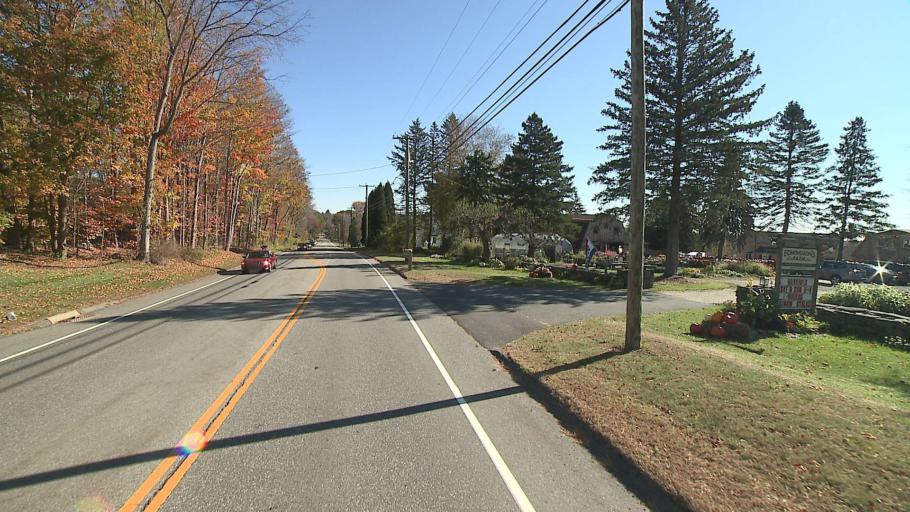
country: US
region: Connecticut
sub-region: Tolland County
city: Coventry Lake
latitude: 41.7962
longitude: -72.4081
